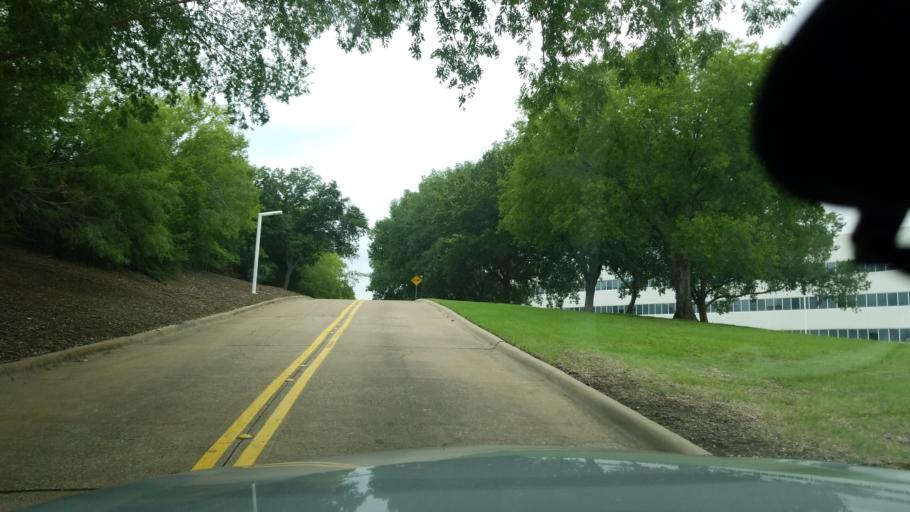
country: US
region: Texas
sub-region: Dallas County
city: Irving
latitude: 32.8532
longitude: -96.9301
